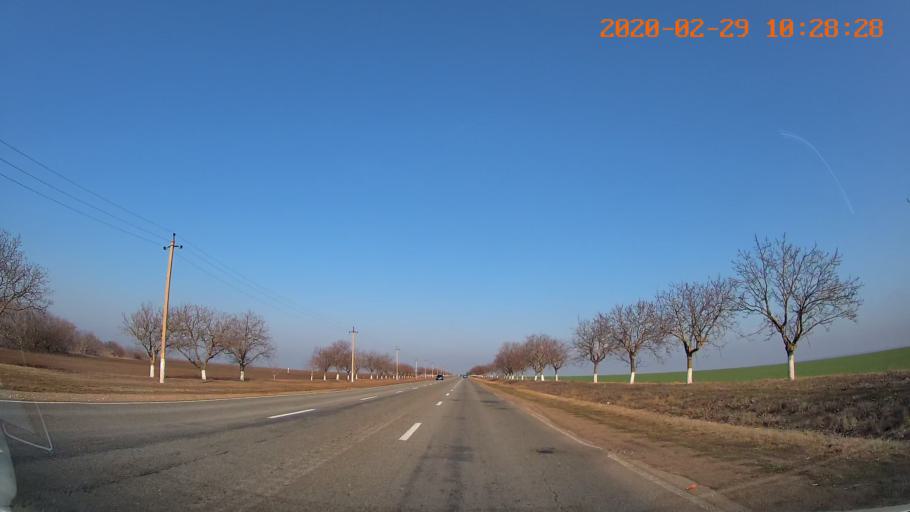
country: MD
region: Telenesti
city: Tiraspolul Nou
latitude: 46.9110
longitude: 29.5912
